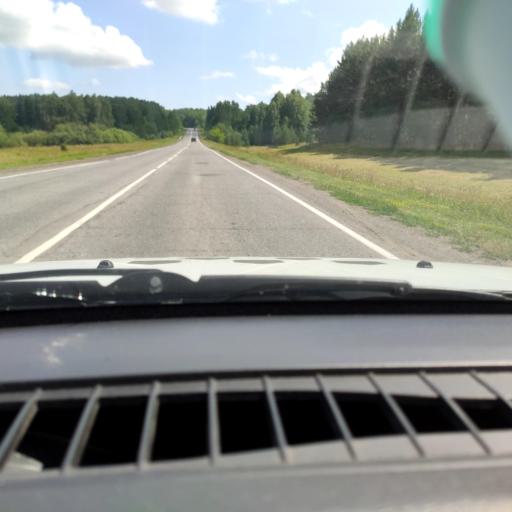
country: RU
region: Bashkortostan
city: Verkhniye Kigi
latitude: 55.3892
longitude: 58.6598
